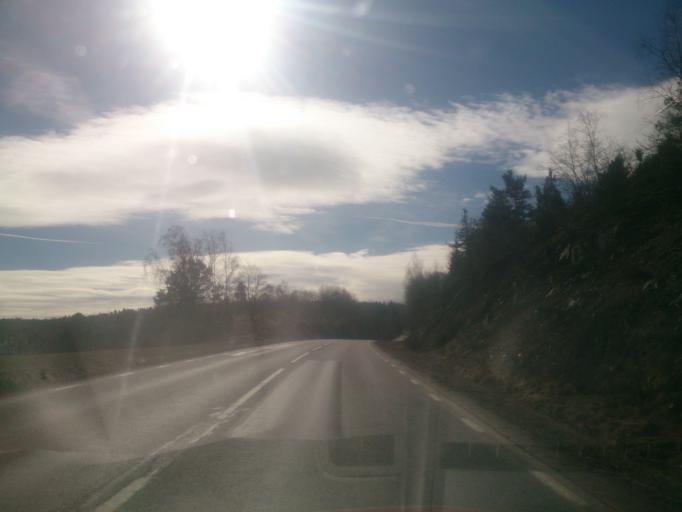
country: SE
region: OEstergoetland
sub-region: Finspangs Kommun
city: Finspang
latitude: 58.6423
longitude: 15.8221
